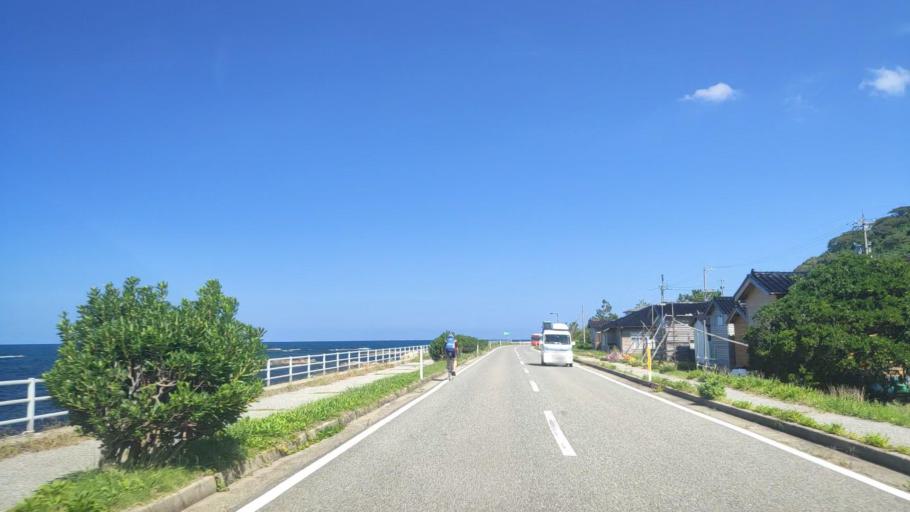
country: JP
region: Ishikawa
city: Nanao
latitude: 37.4841
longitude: 137.1083
